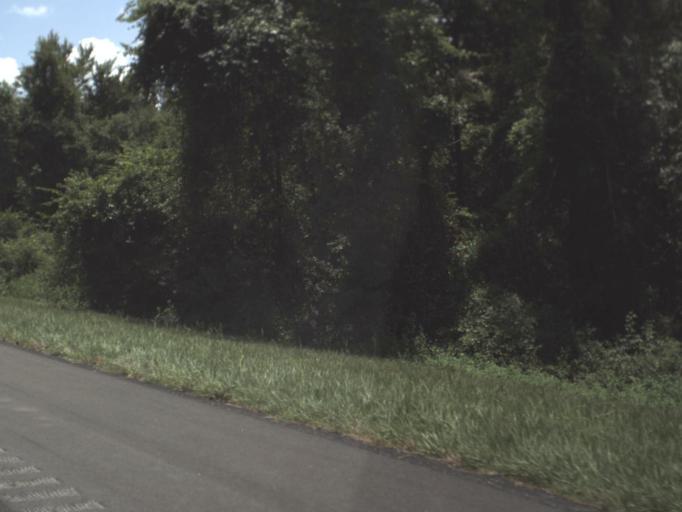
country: US
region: Florida
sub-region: Madison County
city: Madison
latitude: 30.4096
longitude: -83.4173
